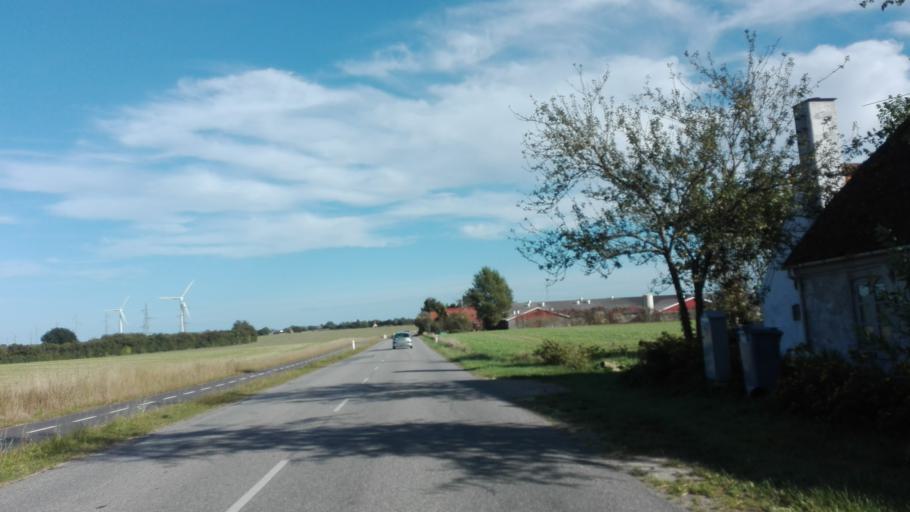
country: DK
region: South Denmark
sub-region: Vejle Kommune
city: Borkop
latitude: 55.5872
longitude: 9.6756
